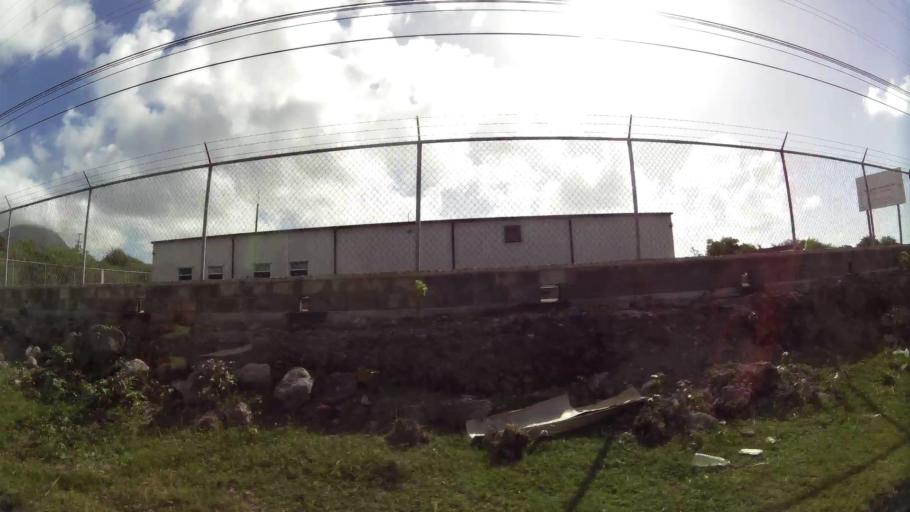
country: KN
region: Saint Paul Charlestown
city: Charlestown
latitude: 17.1182
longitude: -62.6194
